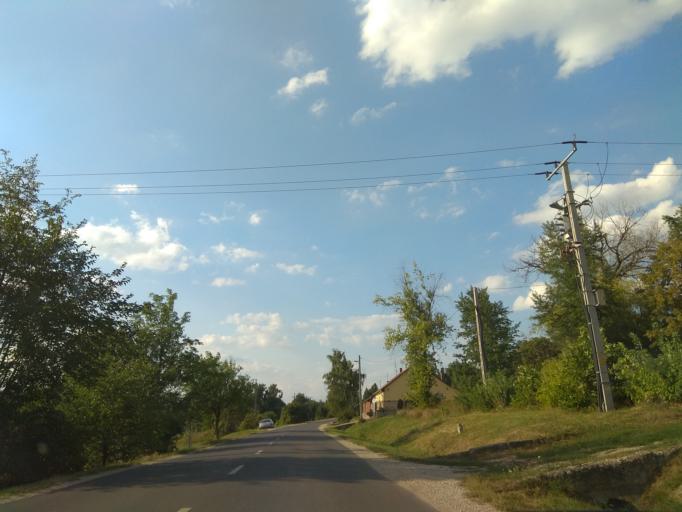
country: HU
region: Borsod-Abauj-Zemplen
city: Harsany
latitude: 47.9559
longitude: 20.7443
